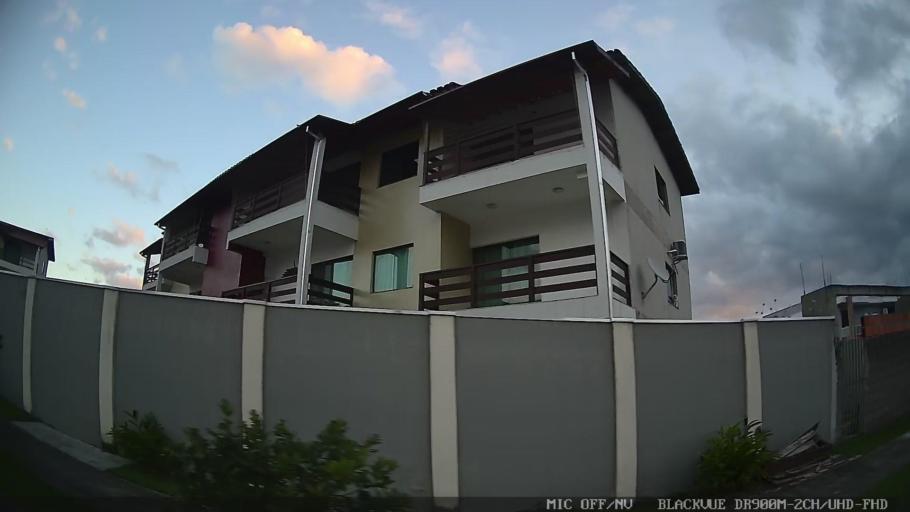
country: BR
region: Sao Paulo
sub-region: Caraguatatuba
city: Caraguatatuba
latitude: -23.6658
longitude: -45.4469
